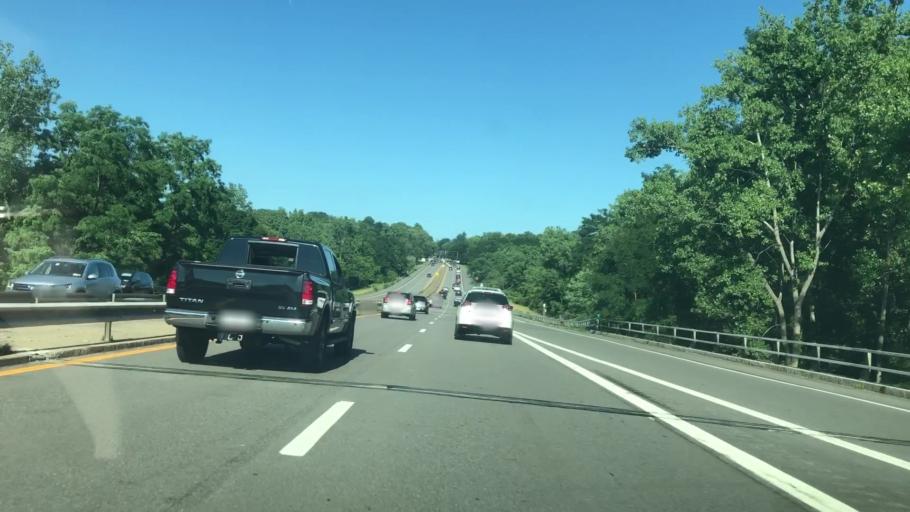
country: US
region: New York
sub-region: Monroe County
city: East Rochester
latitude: 43.1278
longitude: -77.4912
